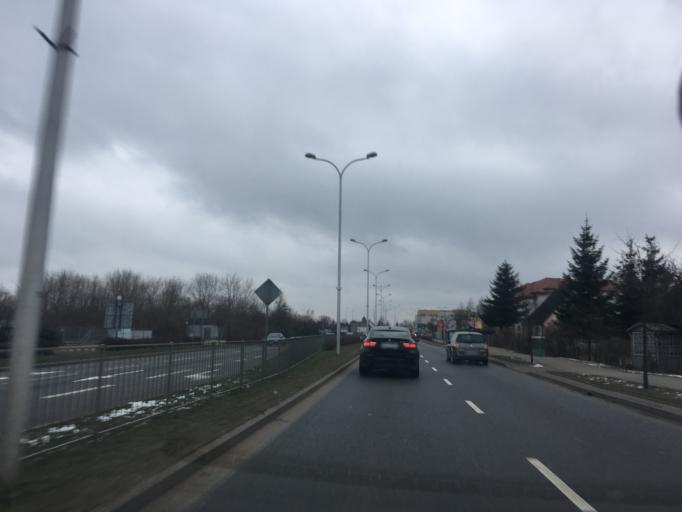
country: PL
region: Podlasie
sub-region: Suwalki
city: Suwalki
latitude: 54.1136
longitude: 22.9284
